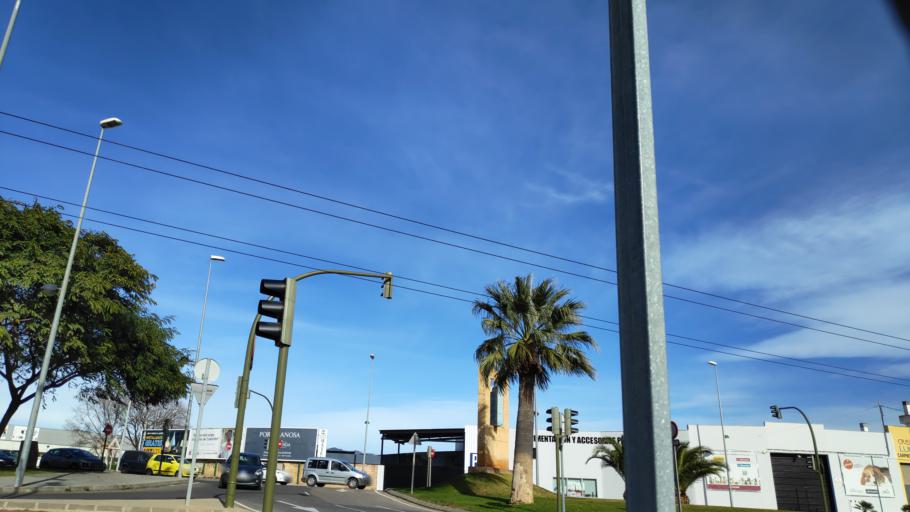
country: ES
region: Valencia
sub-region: Provincia de Castello
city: Castello de la Plana
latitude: 39.9904
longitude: -0.0543
